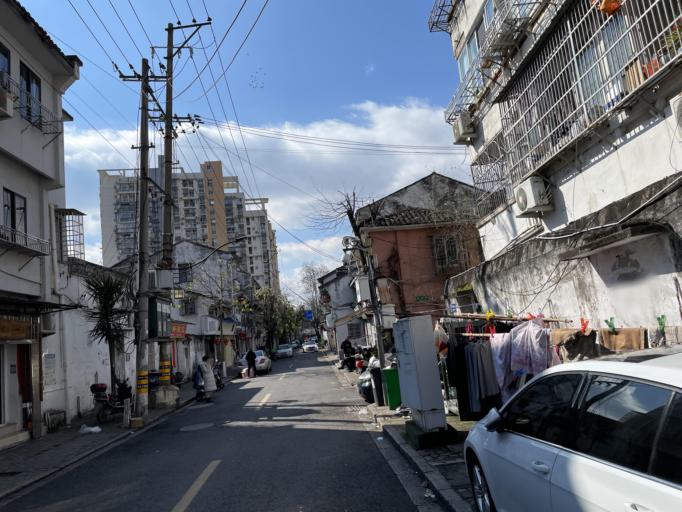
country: CN
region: Zhejiang Sheng
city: Wuma
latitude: 28.0206
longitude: 120.6487
